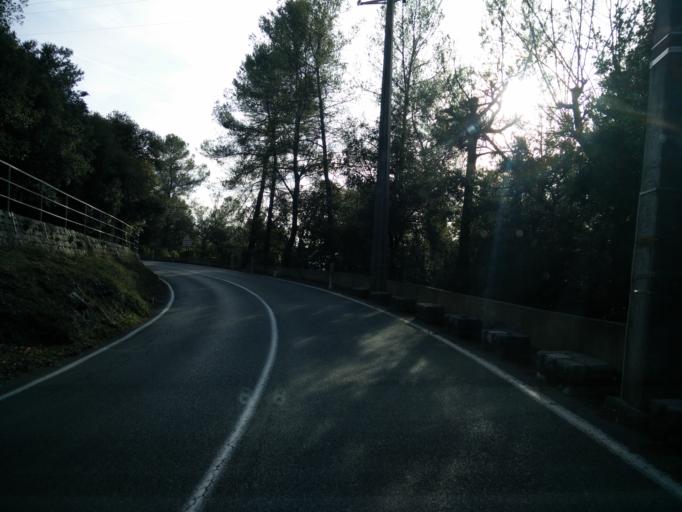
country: FR
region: Provence-Alpes-Cote d'Azur
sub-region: Departement des Alpes-Maritimes
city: Le Tignet
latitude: 43.6326
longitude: 6.8417
